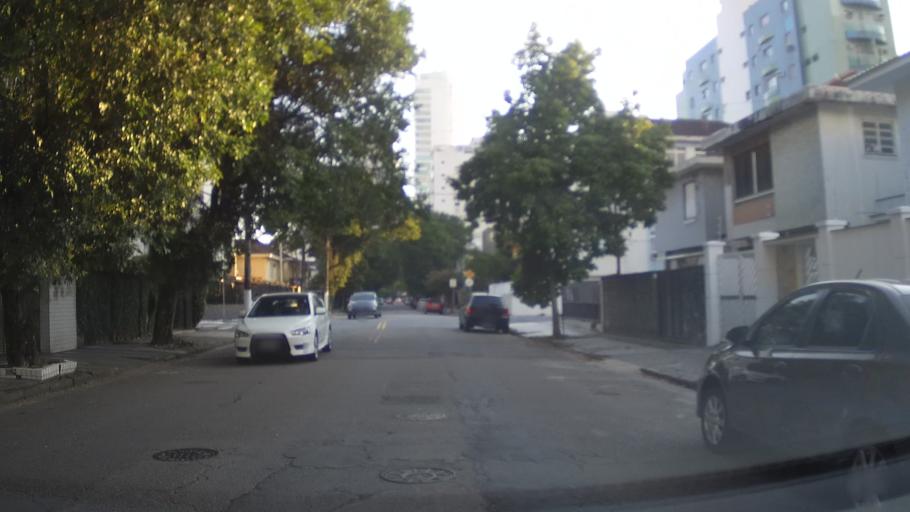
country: BR
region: Sao Paulo
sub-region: Santos
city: Santos
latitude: -23.9832
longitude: -46.3036
